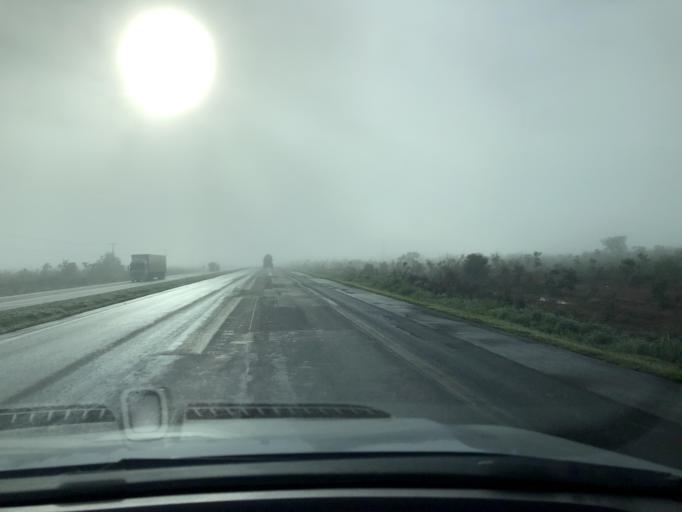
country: BR
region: Goias
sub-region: Luziania
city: Luziania
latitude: -16.2709
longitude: -47.8780
